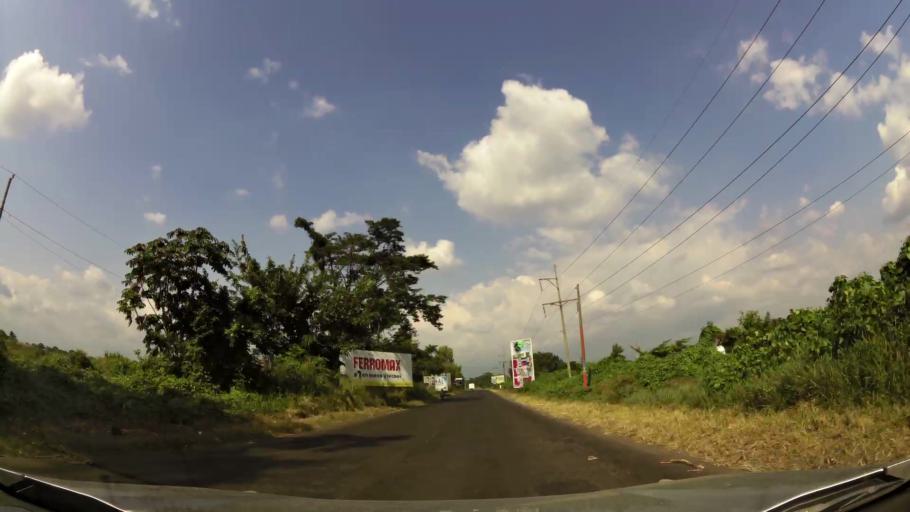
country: GT
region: Retalhuleu
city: San Sebastian
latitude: 14.5643
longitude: -91.6357
